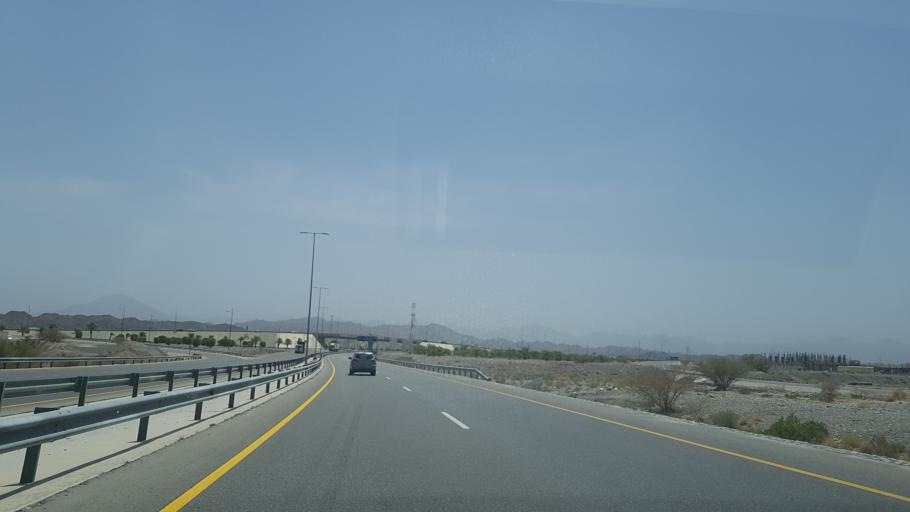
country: OM
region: Muhafazat ad Dakhiliyah
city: Sufalat Sama'il
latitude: 23.2826
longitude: 57.9364
